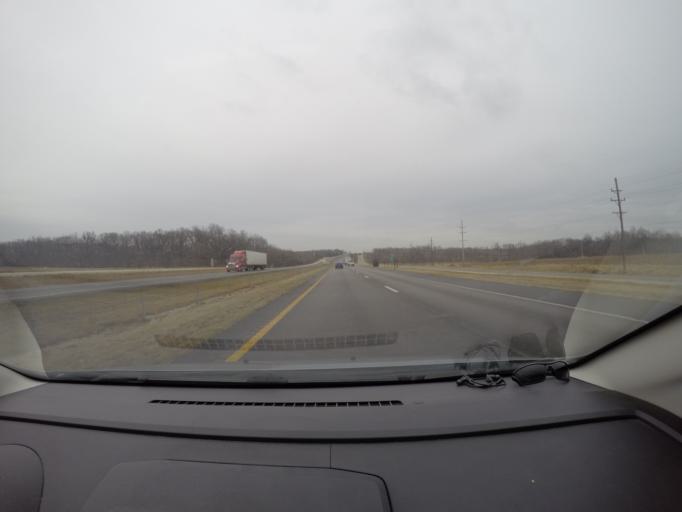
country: US
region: Missouri
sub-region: Warren County
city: Warrenton
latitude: 38.8461
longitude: -91.2478
